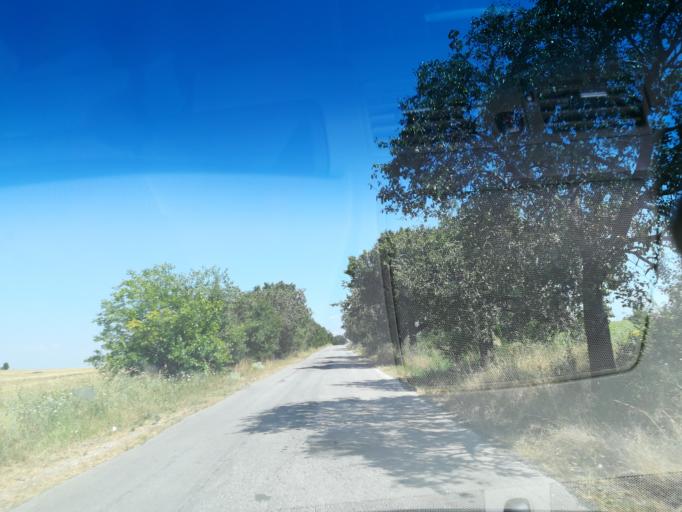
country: BG
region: Plovdiv
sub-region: Obshtina Sadovo
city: Sadovo
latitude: 42.0221
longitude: 25.0171
